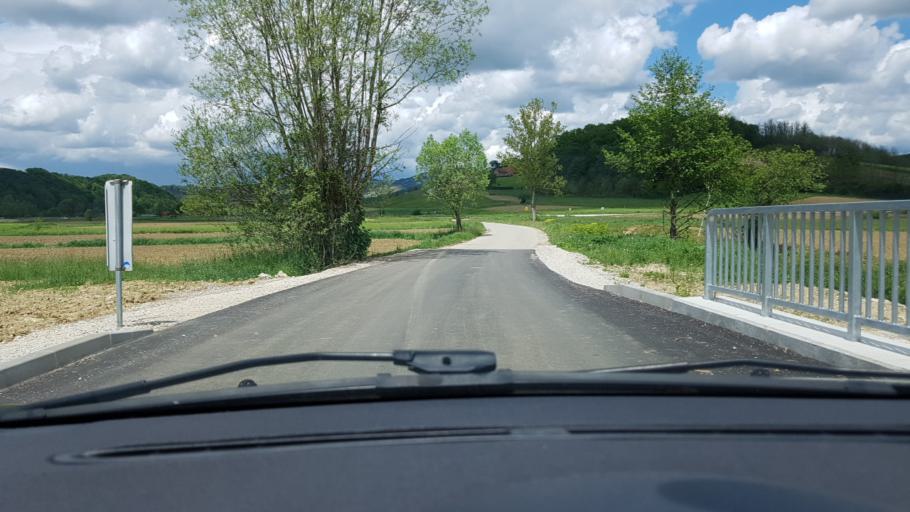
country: HR
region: Krapinsko-Zagorska
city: Pregrada
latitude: 46.1392
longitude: 15.8131
